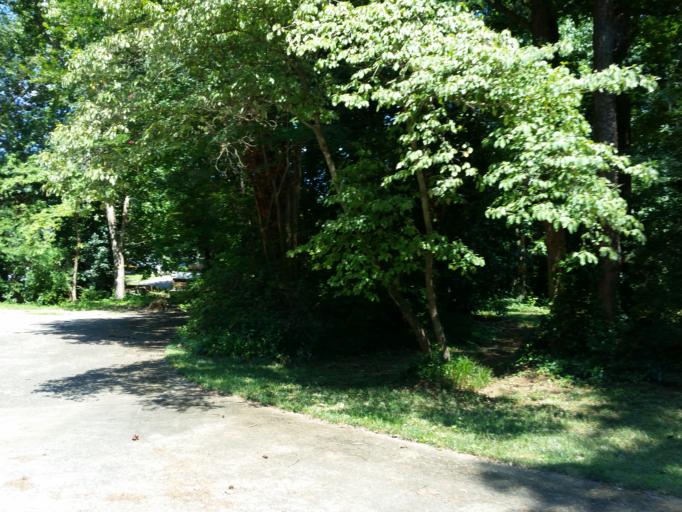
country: US
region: Georgia
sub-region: Cobb County
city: Smyrna
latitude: 33.9376
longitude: -84.4757
